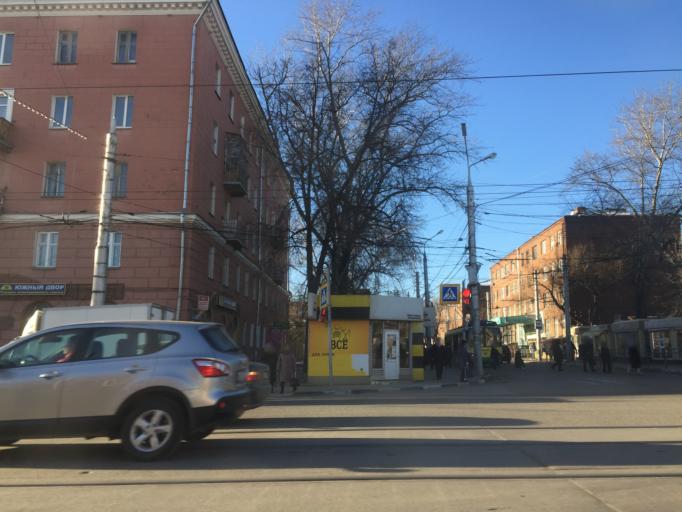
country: RU
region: Tula
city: Tula
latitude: 54.2057
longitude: 37.6190
